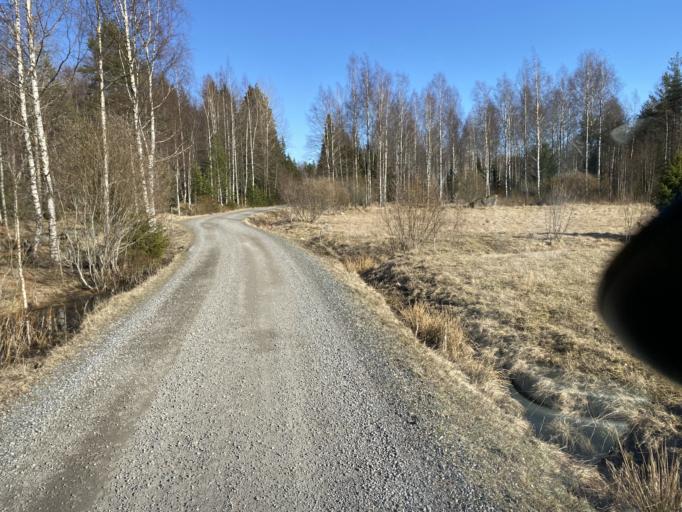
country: FI
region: Satakunta
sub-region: Rauma
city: Lappi
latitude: 61.1477
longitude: 21.9033
